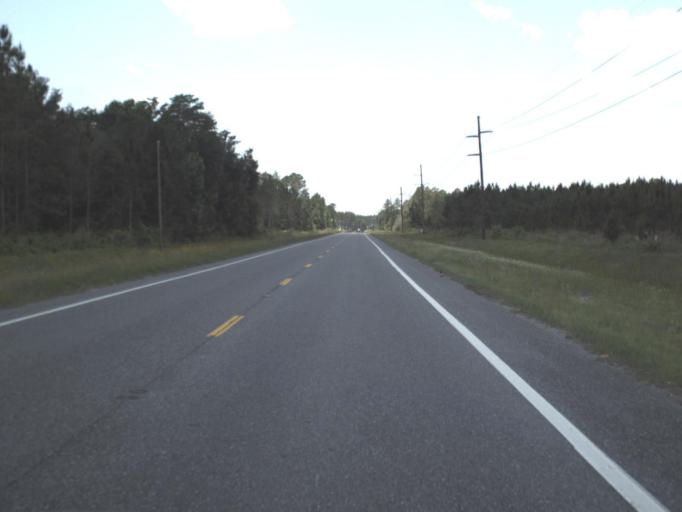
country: US
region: Florida
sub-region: Union County
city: Lake Butler
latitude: 29.9812
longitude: -82.2394
